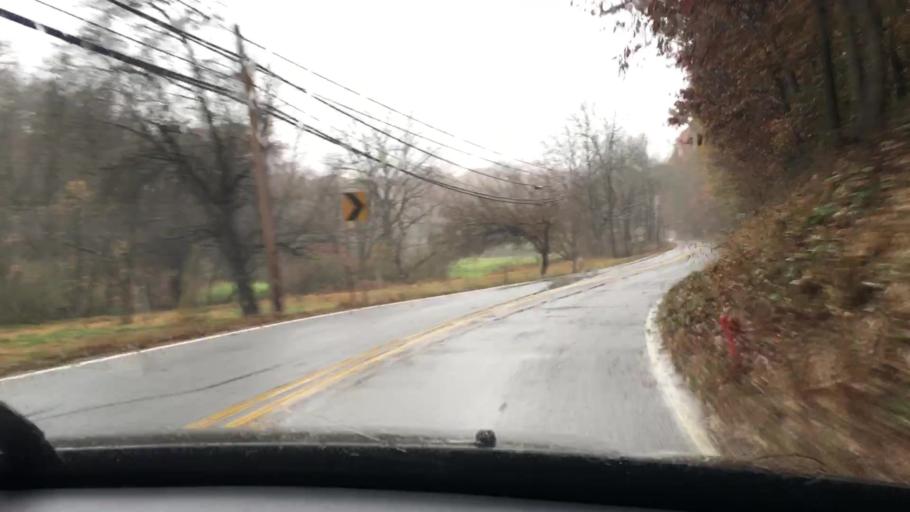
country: US
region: Pennsylvania
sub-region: York County
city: Glen Rock
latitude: 39.7727
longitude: -76.7175
